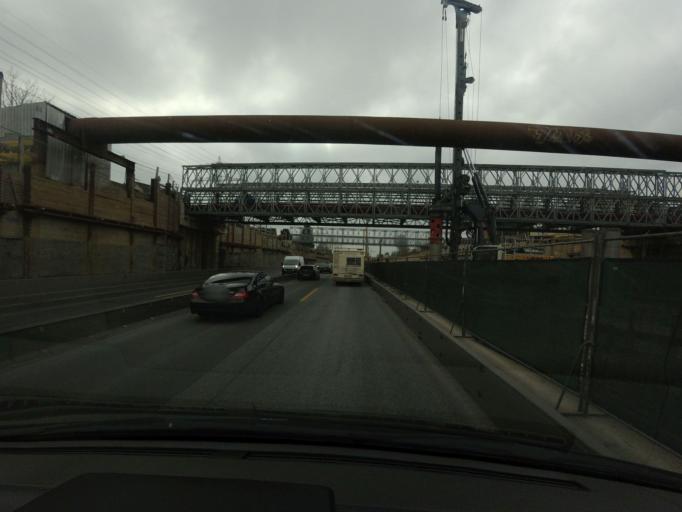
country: DE
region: Hamburg
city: Eidelstedt
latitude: 53.6320
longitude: 9.9230
